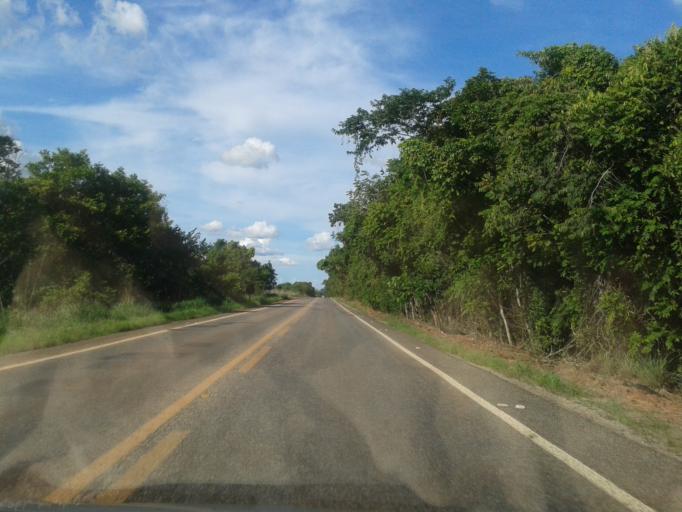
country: BR
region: Goias
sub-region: Mozarlandia
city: Mozarlandia
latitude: -14.4402
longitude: -50.4583
